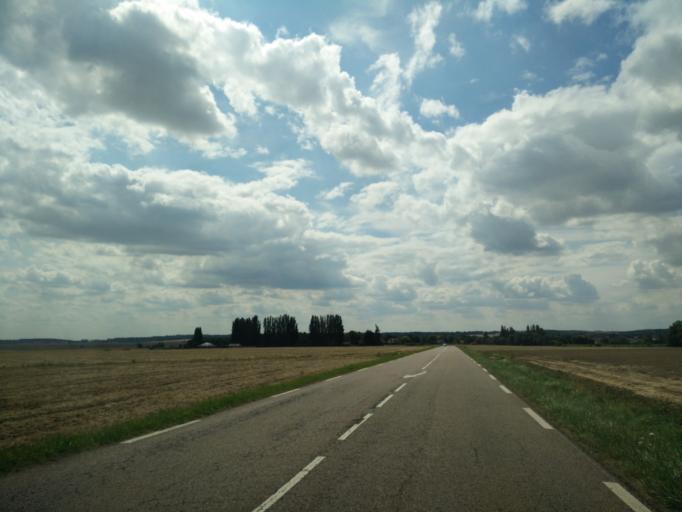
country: FR
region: Ile-de-France
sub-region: Departement des Yvelines
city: Guerville
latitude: 48.9209
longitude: 1.7314
